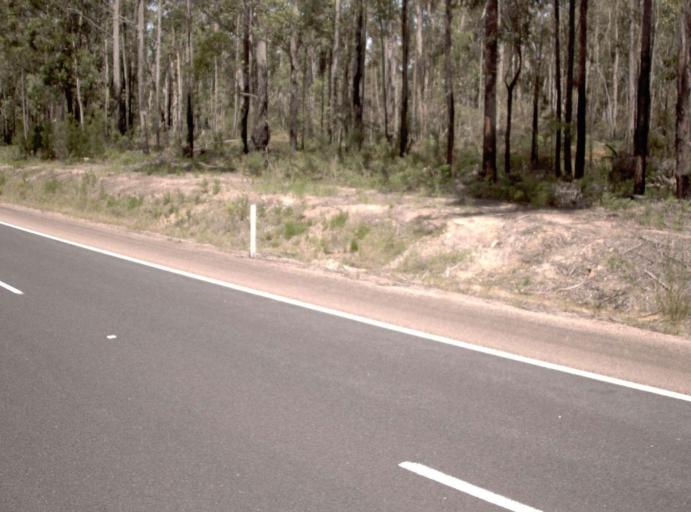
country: AU
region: New South Wales
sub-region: Bombala
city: Bombala
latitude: -37.5684
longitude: 149.2631
